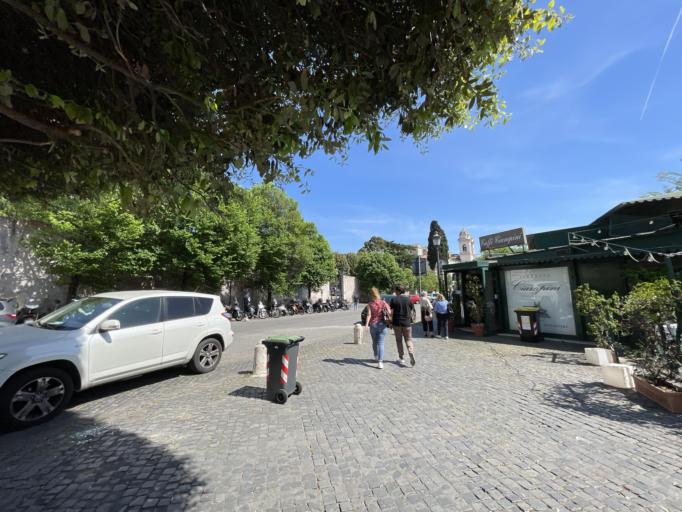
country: VA
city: Vatican City
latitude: 41.9079
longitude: 12.4825
